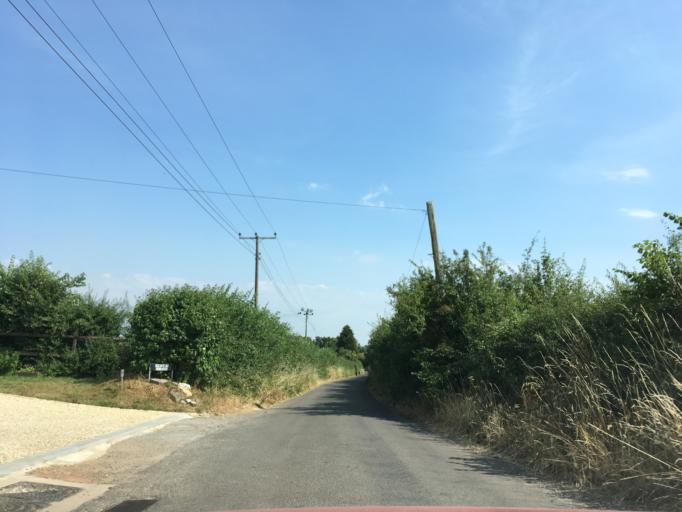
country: GB
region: England
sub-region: South Gloucestershire
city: Tytherington
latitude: 51.5788
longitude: -2.5024
